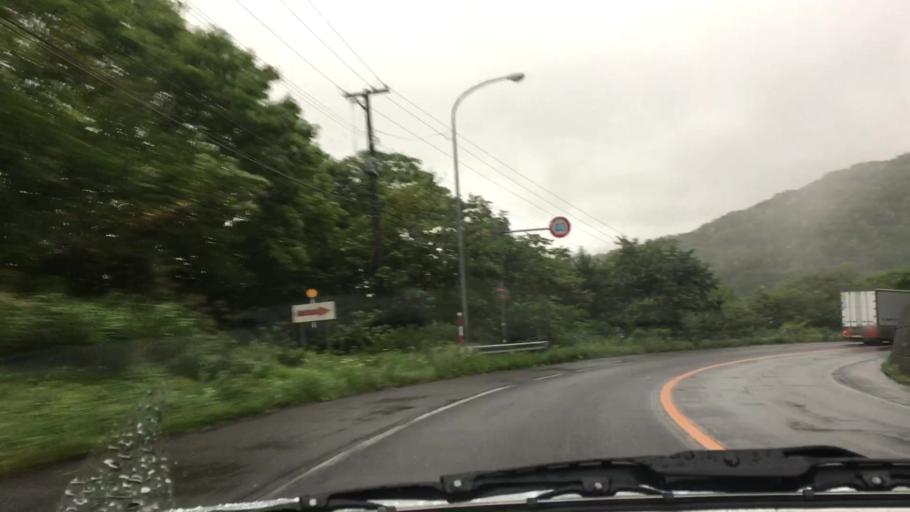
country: JP
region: Hokkaido
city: Niseko Town
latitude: 42.5917
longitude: 140.5913
